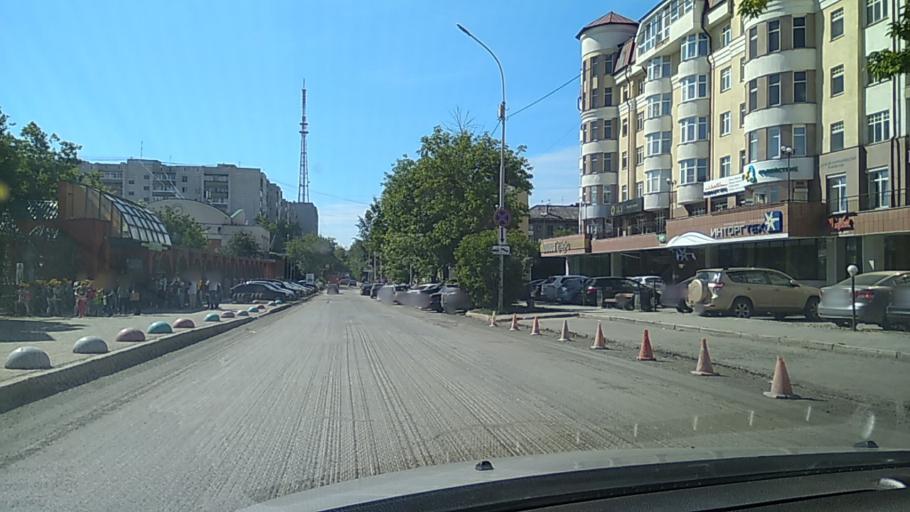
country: RU
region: Sverdlovsk
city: Yekaterinburg
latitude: 56.8331
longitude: 60.6204
